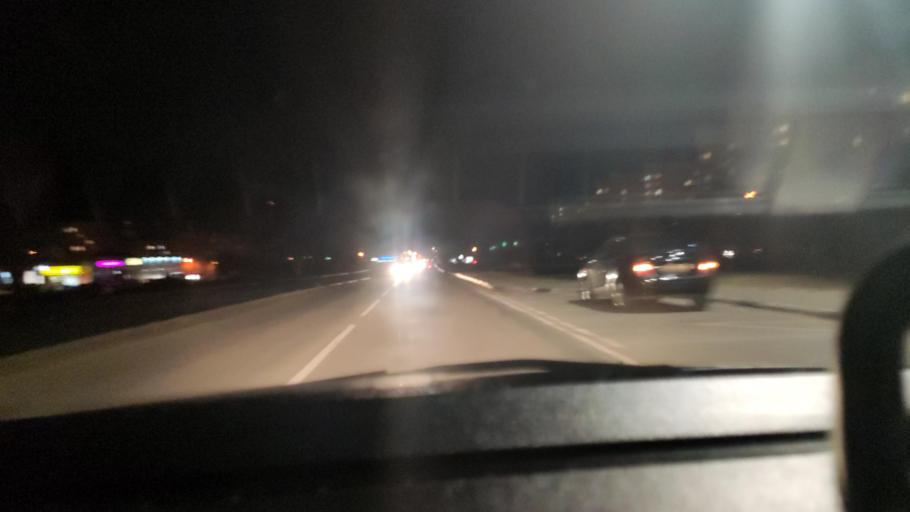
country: RU
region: Voronezj
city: Shilovo
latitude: 51.5627
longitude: 39.1165
